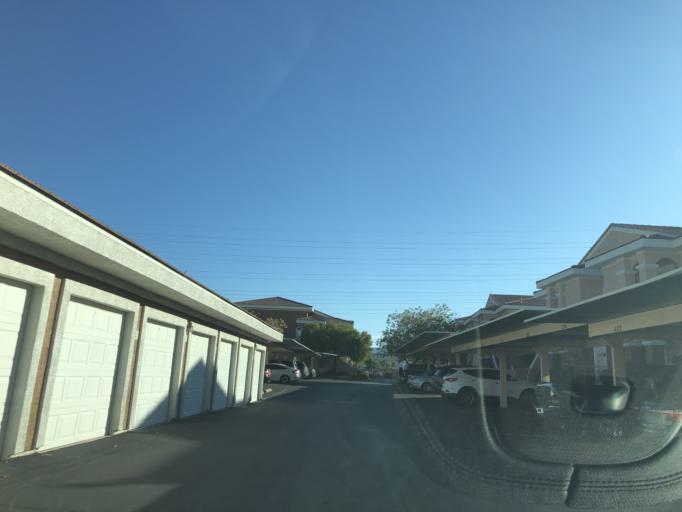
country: US
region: Nevada
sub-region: Clark County
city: Whitney
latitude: 36.0011
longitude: -115.0918
